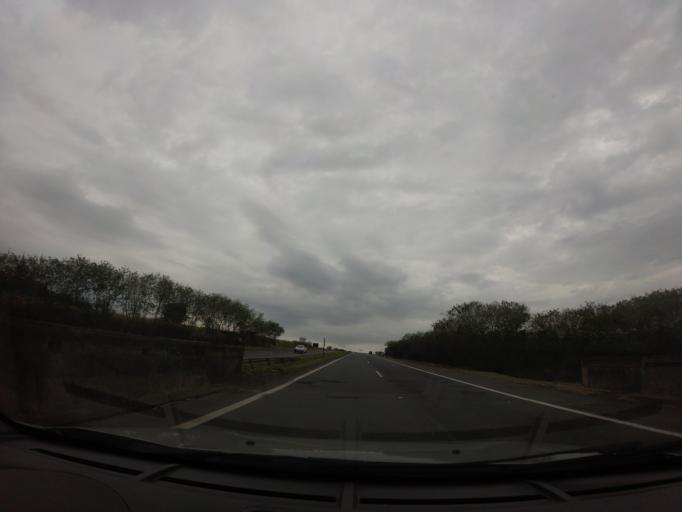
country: BR
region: Sao Paulo
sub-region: Piracicaba
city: Piracicaba
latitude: -22.7269
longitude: -47.5562
